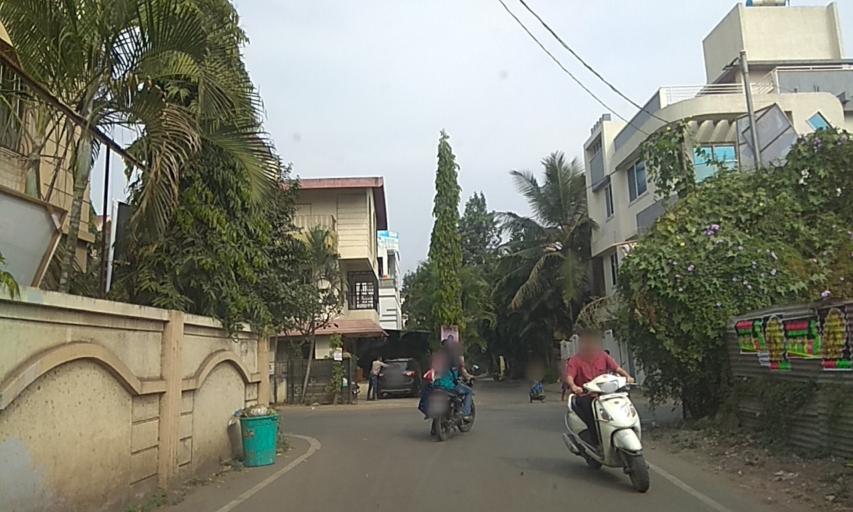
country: IN
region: Maharashtra
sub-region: Pune Division
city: Pune
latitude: 18.5040
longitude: 73.9317
